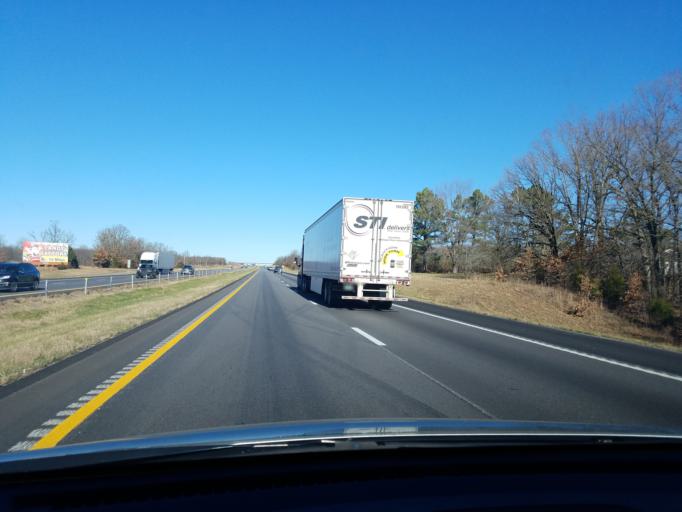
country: US
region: Missouri
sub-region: Webster County
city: Marshfield
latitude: 37.3723
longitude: -92.9059
